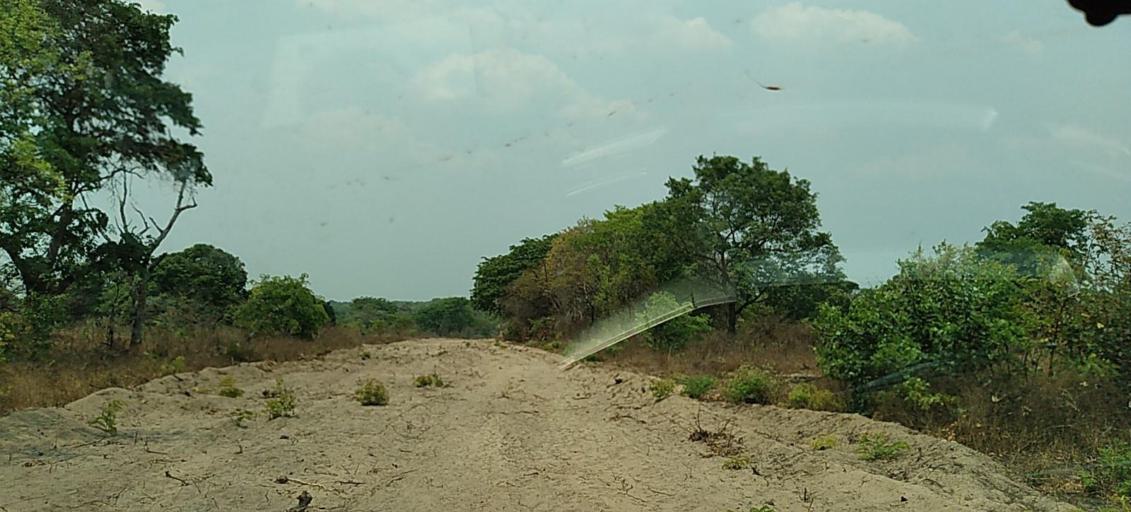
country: ZM
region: Western
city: Lukulu
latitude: -14.0045
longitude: 23.5858
